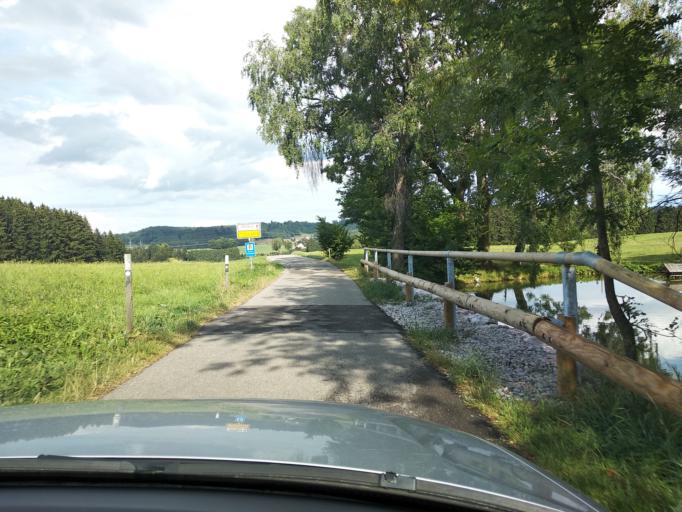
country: DE
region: Bavaria
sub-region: Swabia
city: Wolfertschwenden
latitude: 47.8616
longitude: 10.2496
